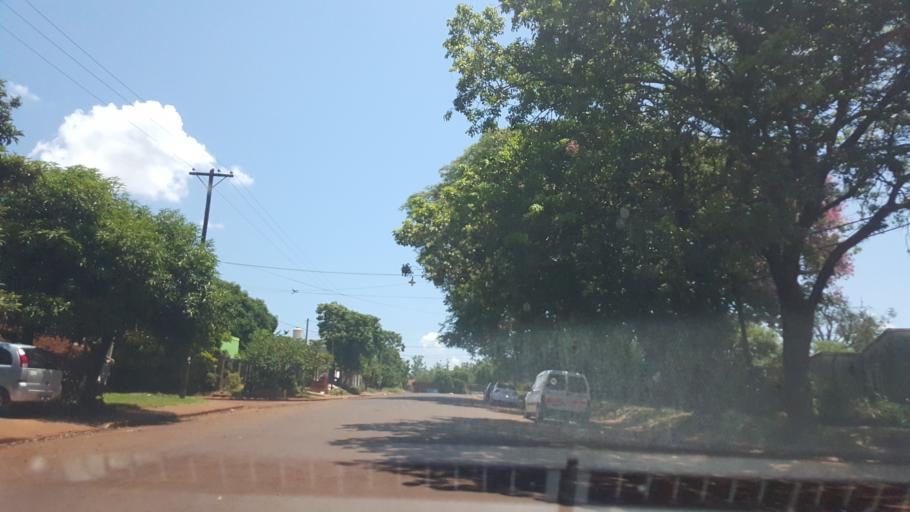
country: AR
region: Misiones
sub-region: Departamento de Capital
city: Posadas
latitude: -27.4059
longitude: -55.9211
